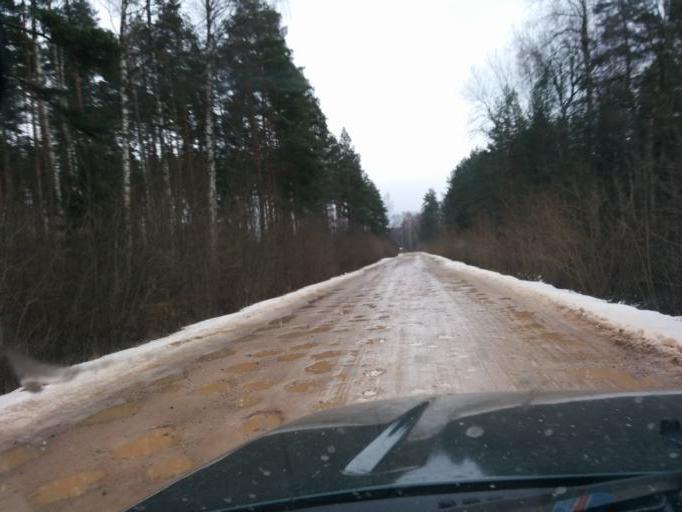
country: LV
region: Ozolnieku
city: Ozolnieki
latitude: 56.6838
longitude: 23.7760
